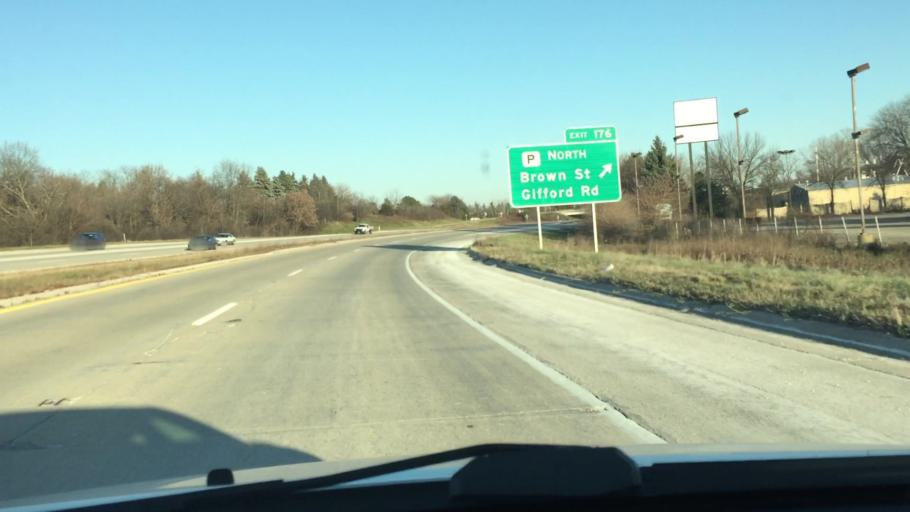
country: US
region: Wisconsin
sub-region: Waukesha County
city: Okauchee Lake
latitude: 43.1077
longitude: -88.4674
